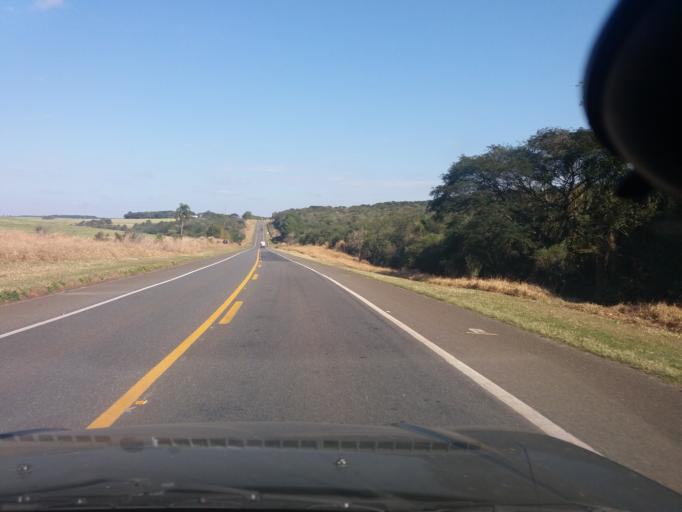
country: BR
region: Sao Paulo
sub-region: Capao Bonito
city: Capao Bonito
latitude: -23.9577
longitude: -48.4654
